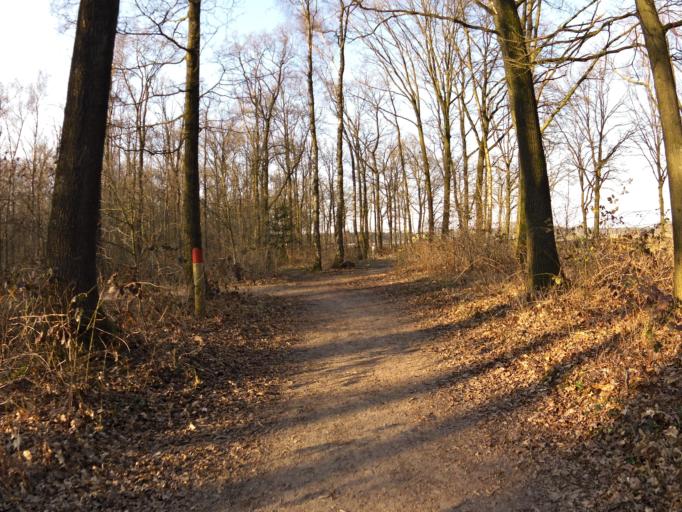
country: NL
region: North Brabant
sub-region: Gemeente Maasdonk
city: Geffen
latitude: 51.7078
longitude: 5.4010
